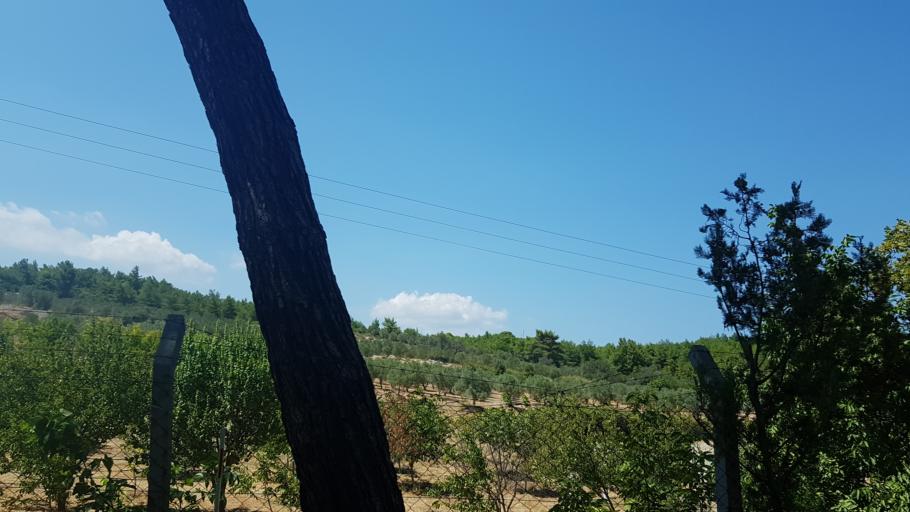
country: TR
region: Izmir
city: Urla
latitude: 38.2424
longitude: 26.7025
